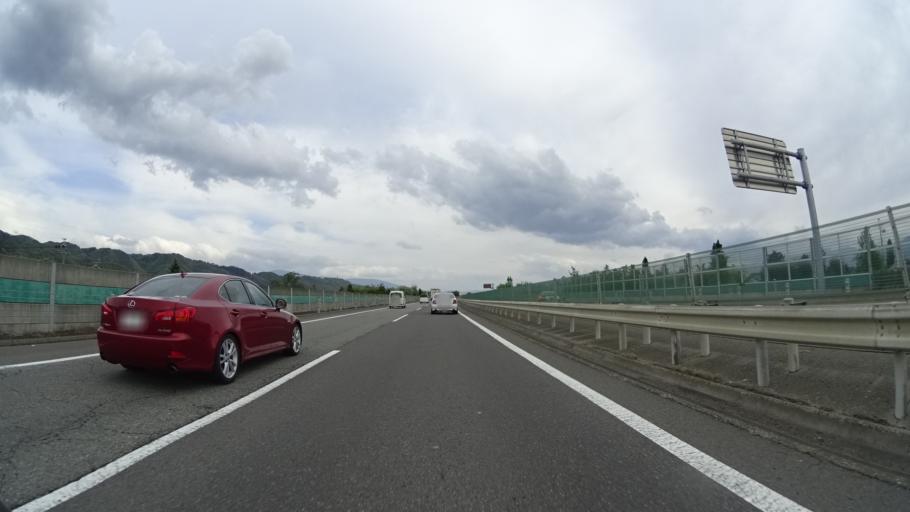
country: JP
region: Nagano
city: Toyoshina
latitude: 36.2958
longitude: 137.9265
